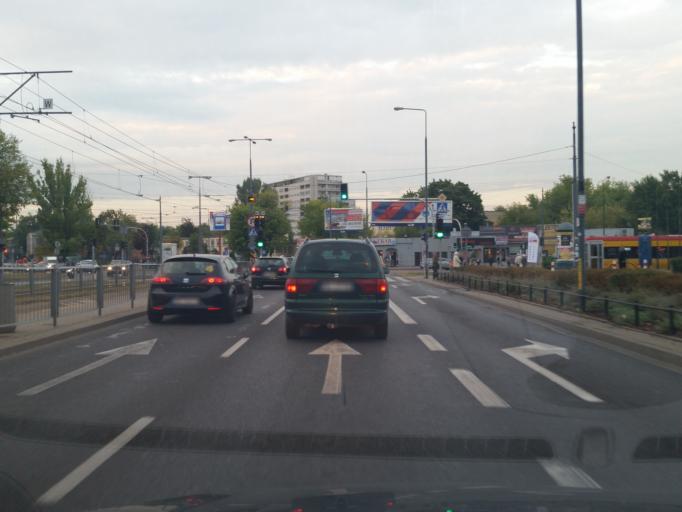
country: PL
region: Masovian Voivodeship
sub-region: Warszawa
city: Bielany
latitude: 52.2747
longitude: 20.9376
